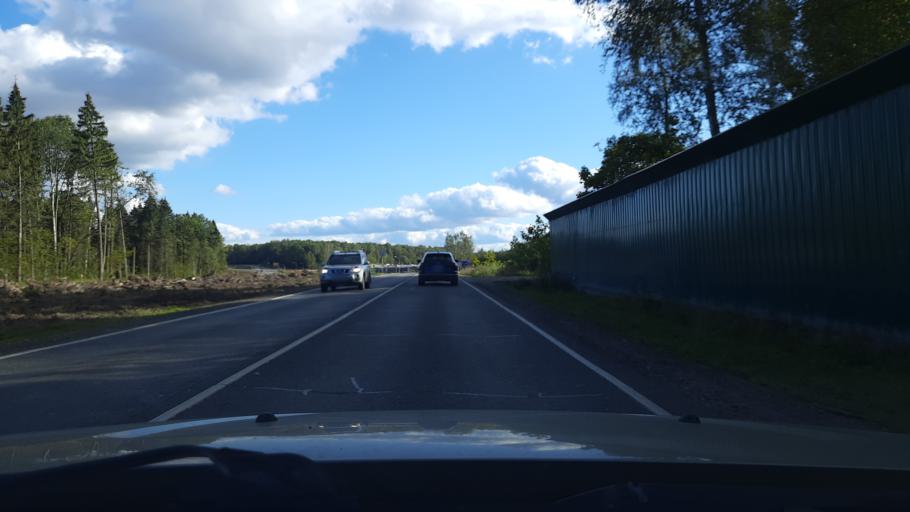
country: RU
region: Moskovskaya
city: Odintsovo
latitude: 55.7010
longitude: 37.2256
